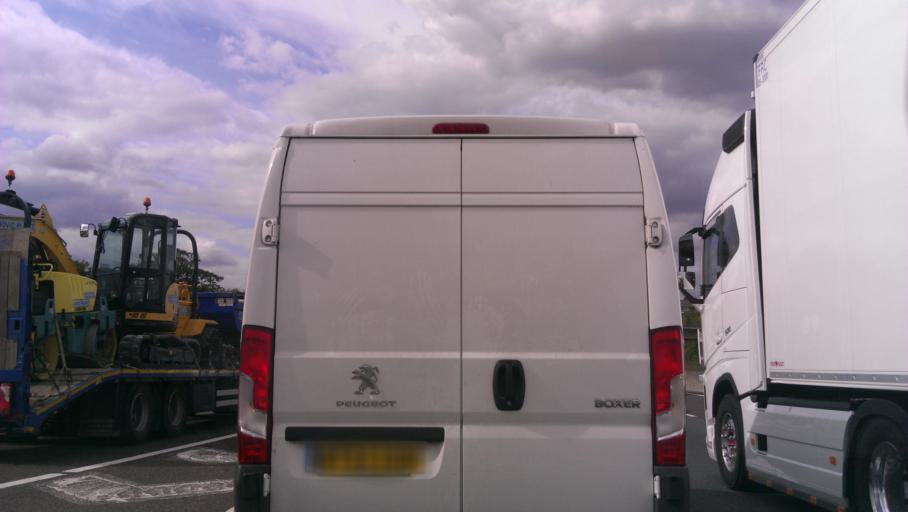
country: GB
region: England
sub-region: Kent
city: Dartford
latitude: 51.4324
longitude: 0.2390
